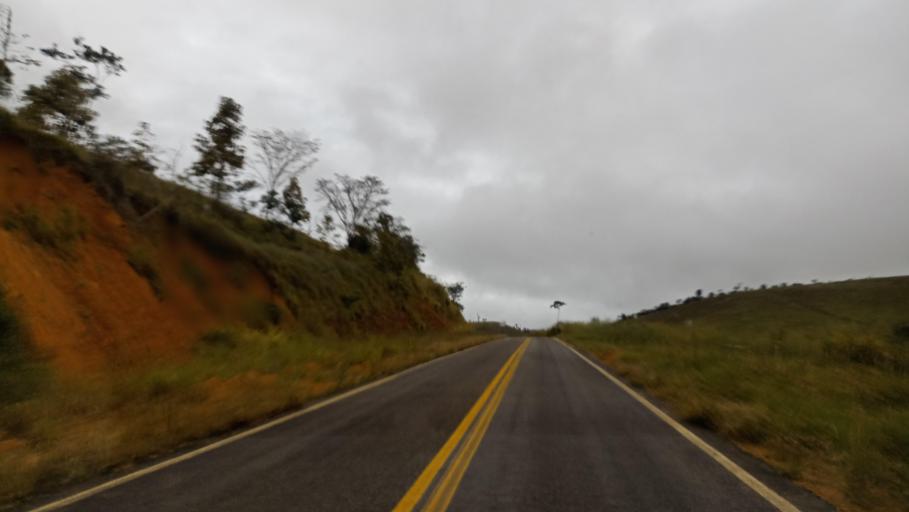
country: BR
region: Minas Gerais
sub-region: Joaima
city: Joaima
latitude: -16.6844
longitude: -40.5222
